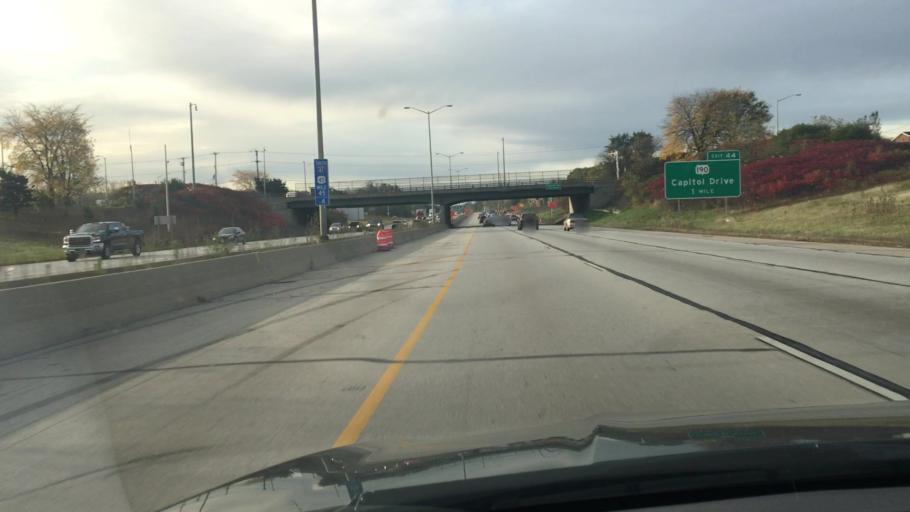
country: US
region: Wisconsin
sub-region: Waukesha County
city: Butler
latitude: 43.1063
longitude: -88.0581
